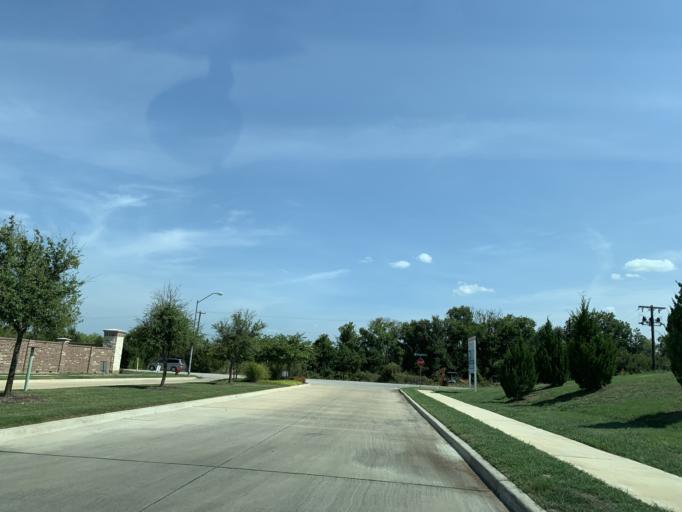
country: US
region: Texas
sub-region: Dallas County
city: Cedar Hill
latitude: 32.6454
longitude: -97.0094
